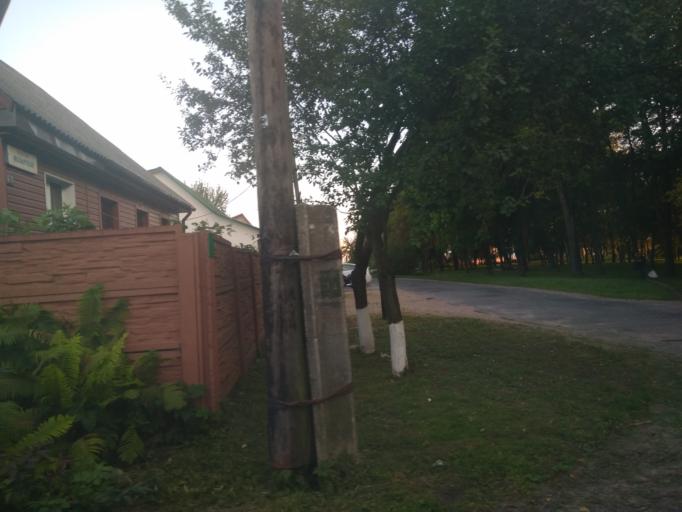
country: BY
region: Minsk
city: Minsk
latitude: 53.9391
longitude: 27.5506
